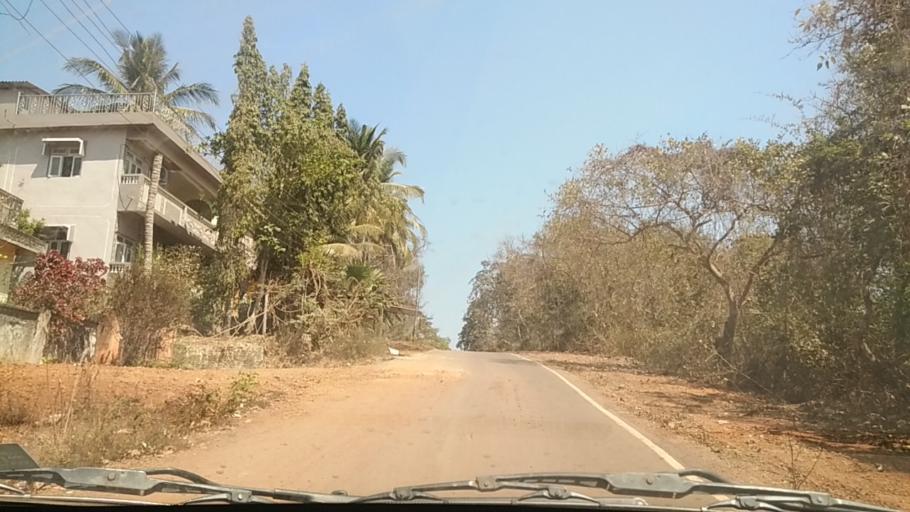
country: IN
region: Goa
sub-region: North Goa
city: Panaji
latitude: 15.5151
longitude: 73.8389
